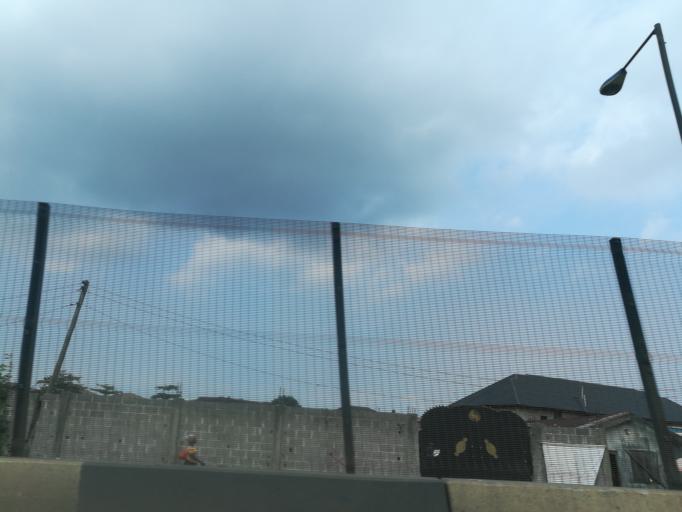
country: NG
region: Lagos
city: Ojota
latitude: 6.5595
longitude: 3.3957
